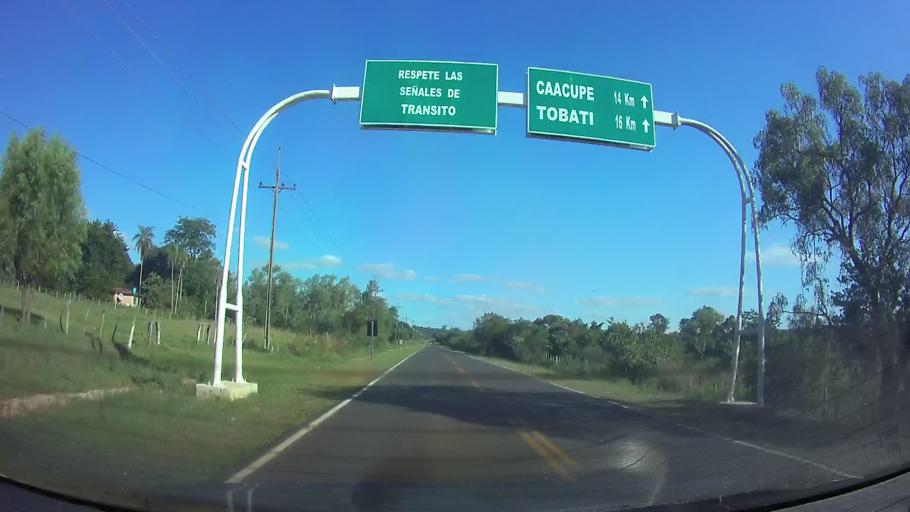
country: PY
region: Cordillera
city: Atyra
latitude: -25.2886
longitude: -57.1693
